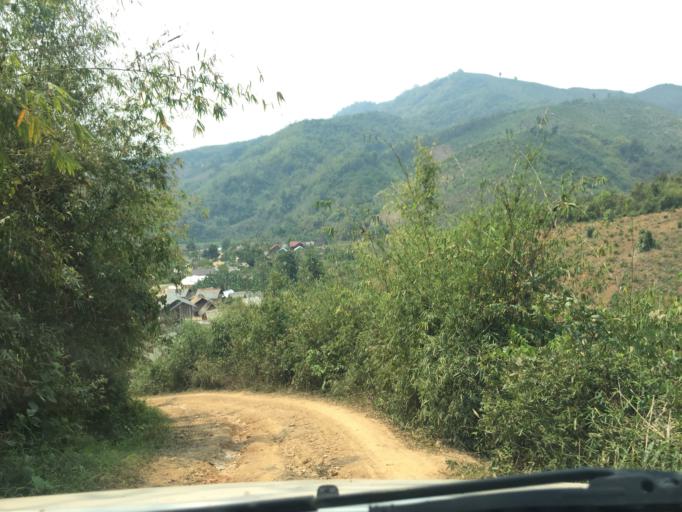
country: LA
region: Loungnamtha
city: Muang Nale
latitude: 20.6022
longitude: 101.5942
